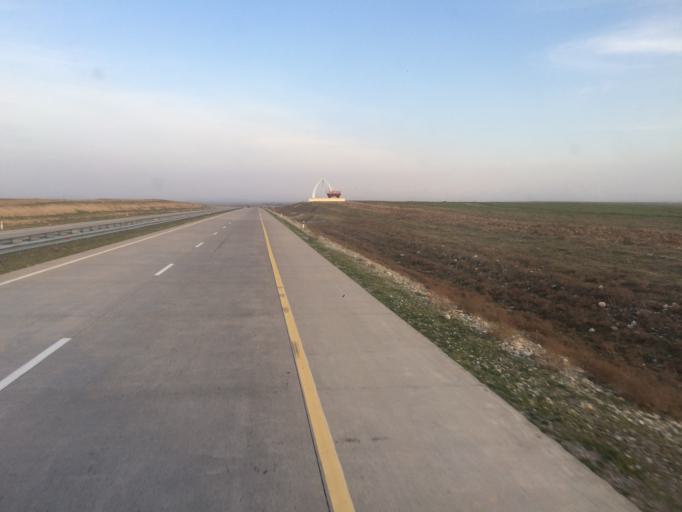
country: KZ
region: Ongtustik Qazaqstan
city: Shymkent
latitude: 42.4938
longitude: 69.4743
